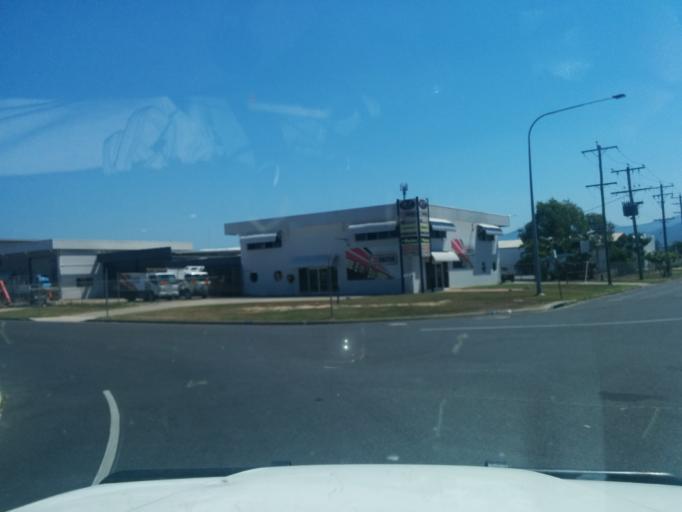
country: AU
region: Queensland
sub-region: Cairns
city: Cairns
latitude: -16.9419
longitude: 145.7723
